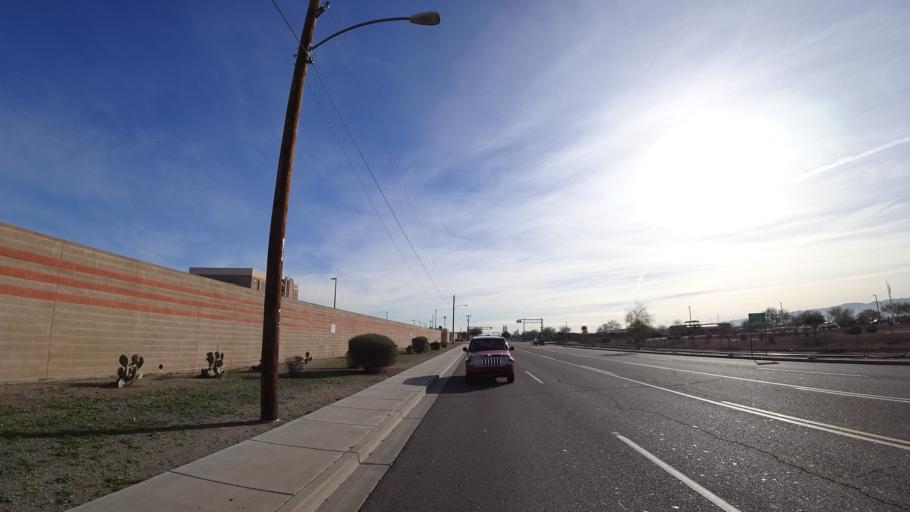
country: US
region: Arizona
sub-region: Maricopa County
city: Phoenix
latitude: 33.4224
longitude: -112.1121
